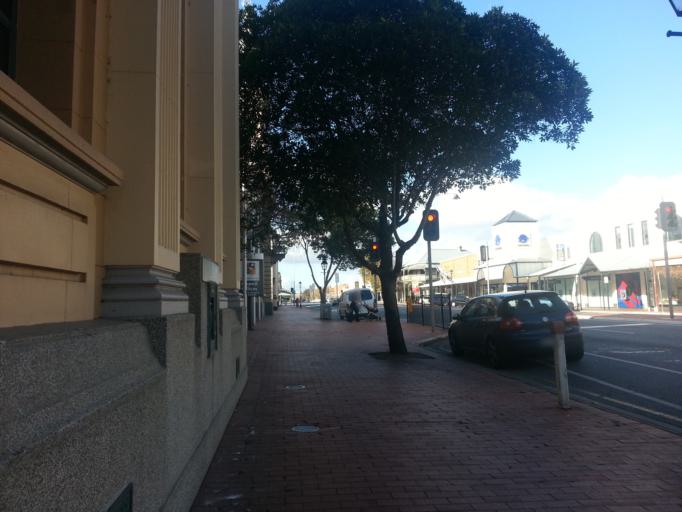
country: AU
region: South Australia
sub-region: Port Adelaide Enfield
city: Birkenhead
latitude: -34.8446
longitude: 138.5036
